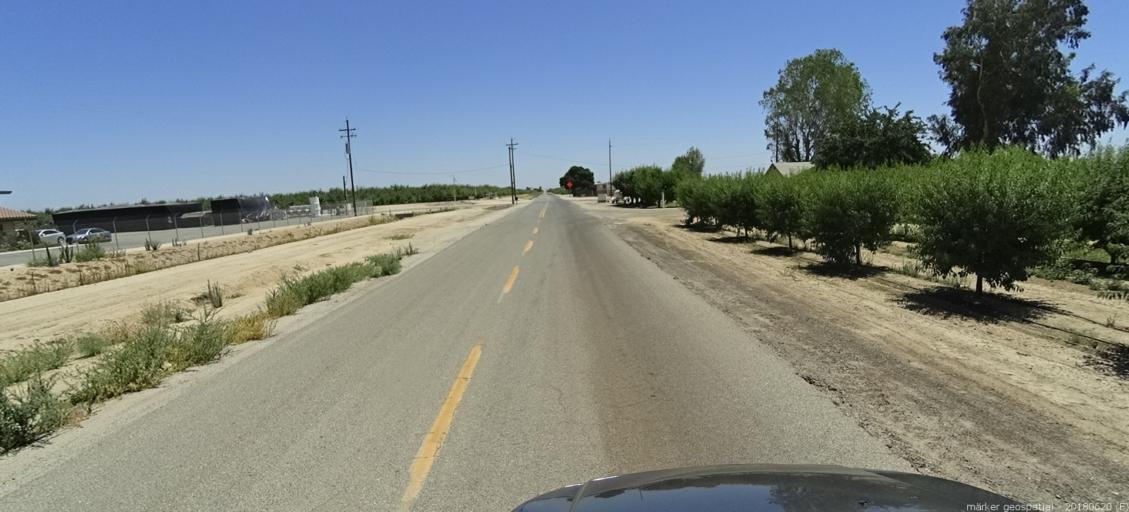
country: US
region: California
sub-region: Fresno County
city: Biola
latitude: 36.8657
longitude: -119.9843
